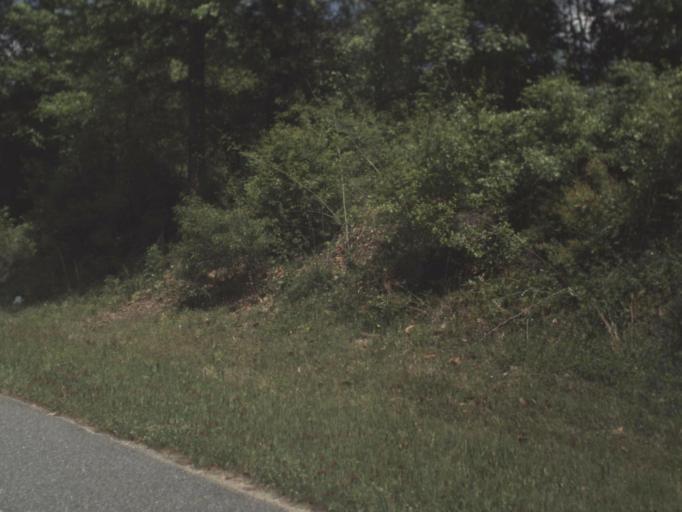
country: US
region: Florida
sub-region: Santa Rosa County
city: Point Baker
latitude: 30.7992
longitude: -87.0416
